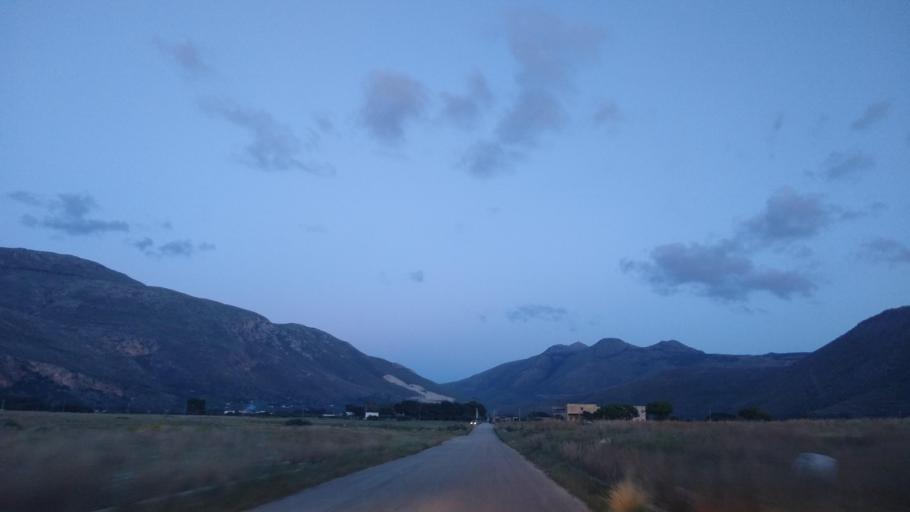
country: IT
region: Sicily
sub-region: Trapani
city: Castelluzzo
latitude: 38.1126
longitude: 12.7220
